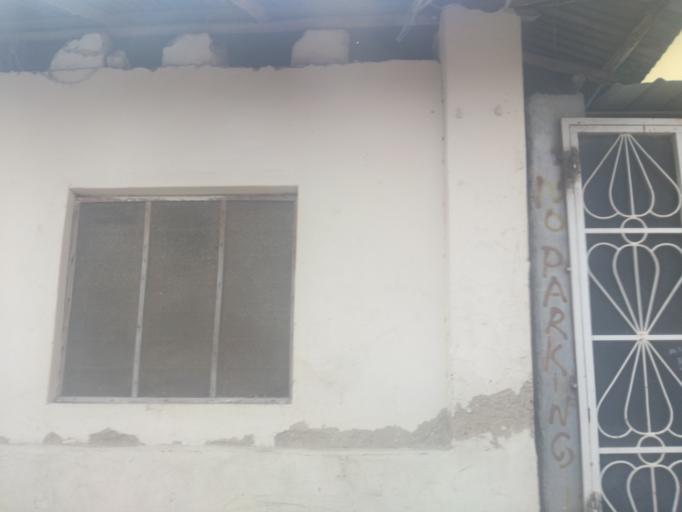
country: TZ
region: Zanzibar Urban/West
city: Zanzibar
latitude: -6.1626
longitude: 39.1980
